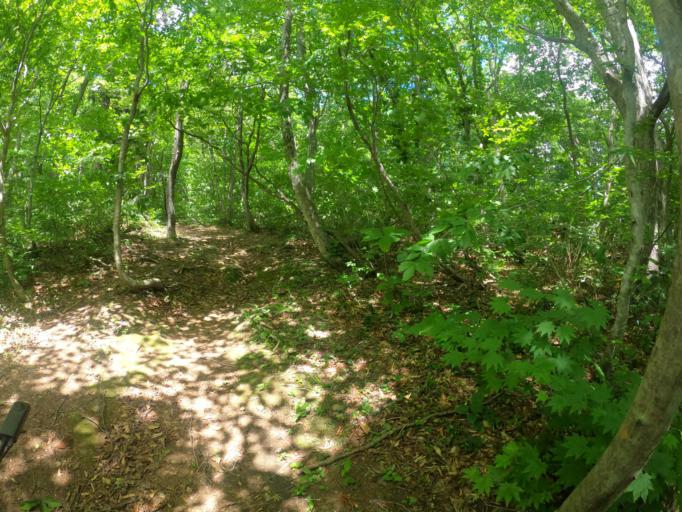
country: JP
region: Iwate
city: Ichinoseki
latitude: 38.9196
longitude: 140.8038
